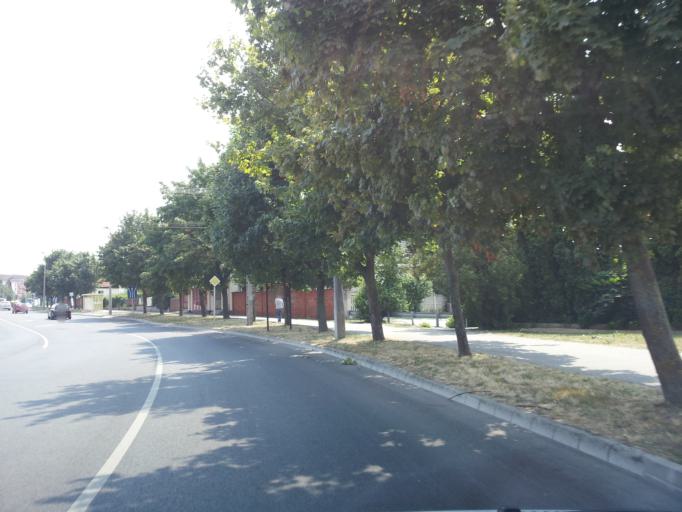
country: HU
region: Veszprem
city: Veszprem
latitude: 47.0997
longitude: 17.9246
